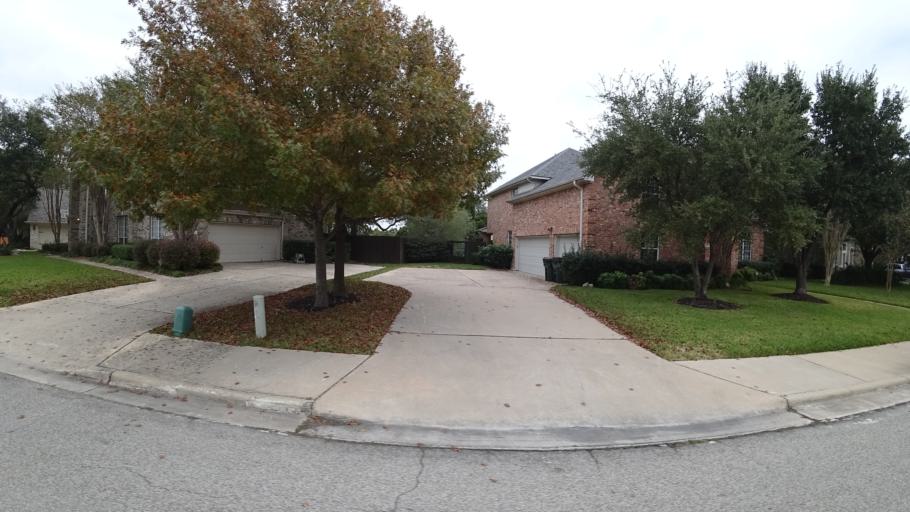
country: US
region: Texas
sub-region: Travis County
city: Bee Cave
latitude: 30.3127
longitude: -97.9311
